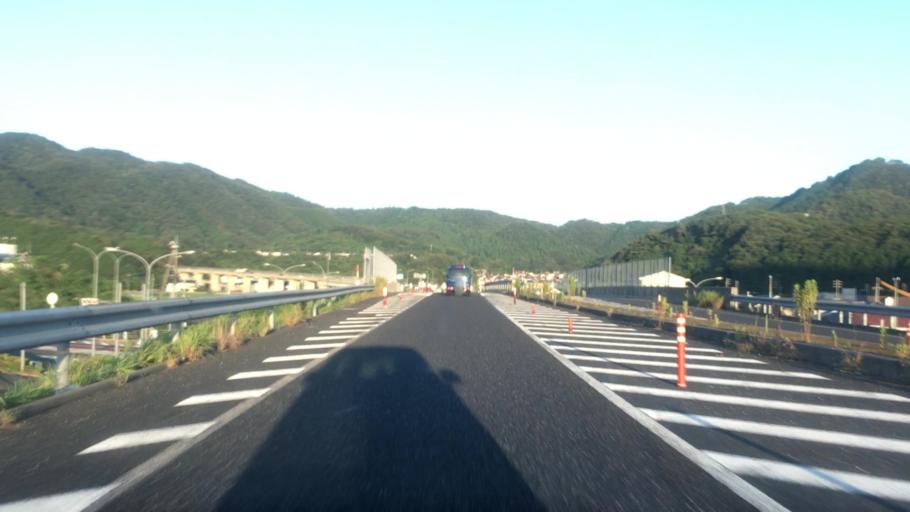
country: JP
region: Tottori
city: Tottori
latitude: 35.5231
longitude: 134.2281
